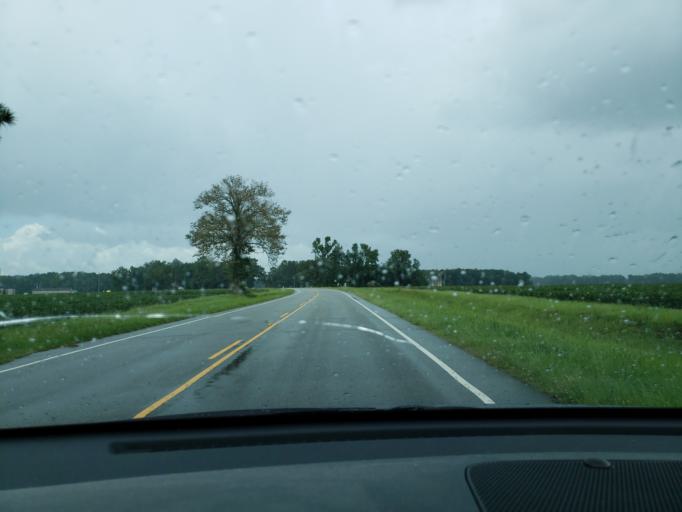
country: US
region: North Carolina
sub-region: Bladen County
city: Elizabethtown
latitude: 34.5113
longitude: -78.6533
